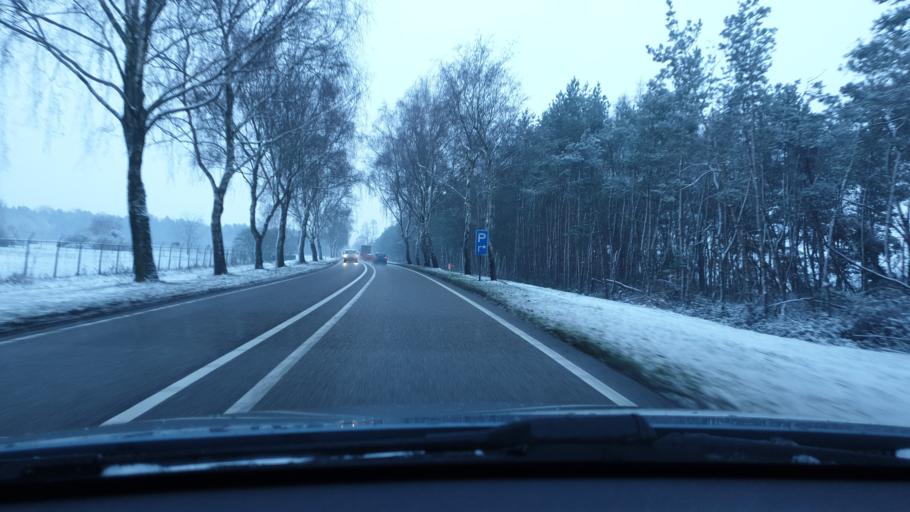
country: NL
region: North Brabant
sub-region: Gemeente Landerd
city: Reek
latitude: 51.7297
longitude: 5.6688
